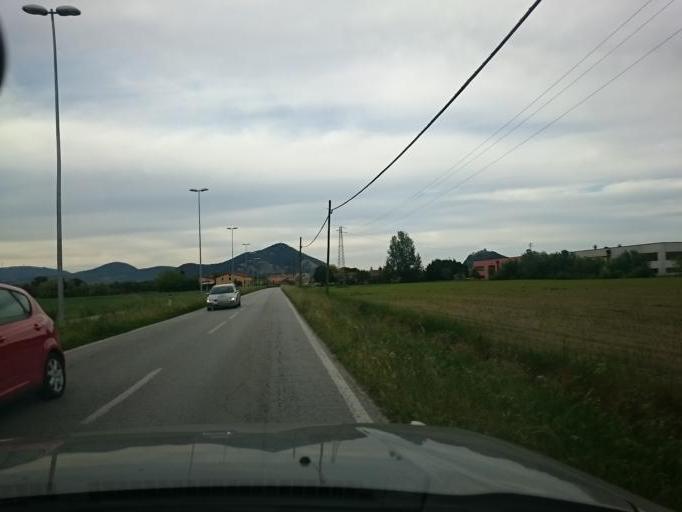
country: IT
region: Veneto
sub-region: Provincia di Padova
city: Monselice
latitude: 45.2184
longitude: 11.7377
